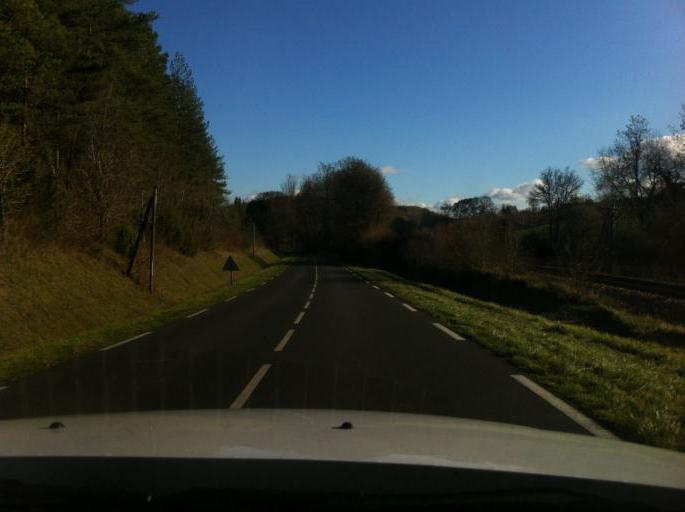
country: FR
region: Aquitaine
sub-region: Departement de la Dordogne
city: Rouffignac-Saint-Cernin-de-Reilhac
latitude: 45.0439
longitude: 0.8828
